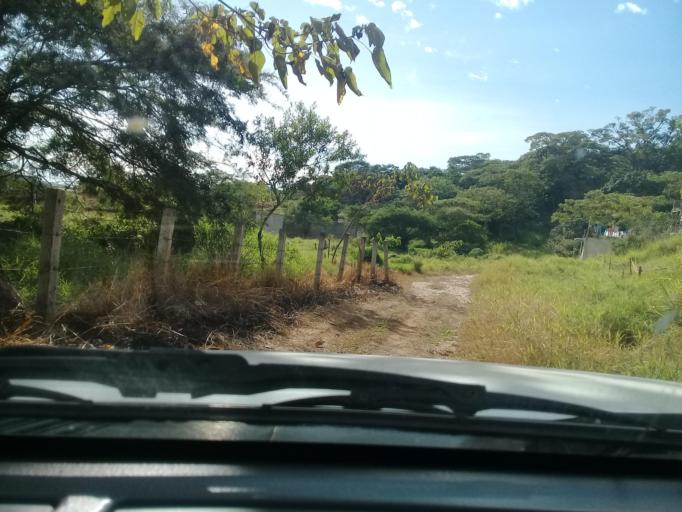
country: MX
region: Veracruz
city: El Castillo
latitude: 19.5431
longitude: -96.8782
